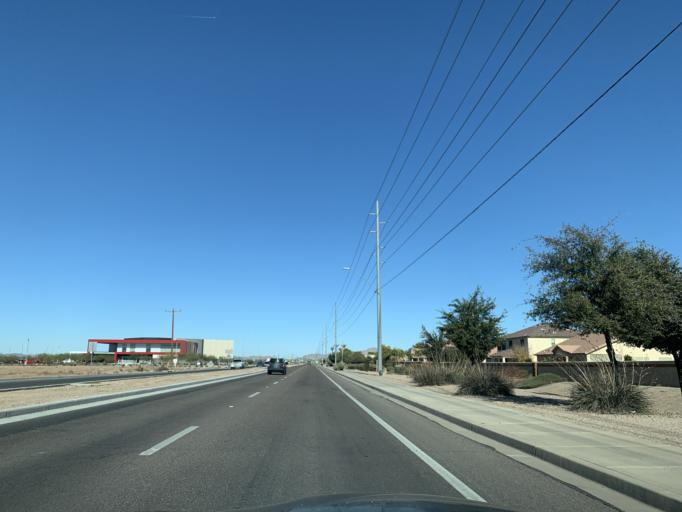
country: US
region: Arizona
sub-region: Pinal County
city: Casa Grande
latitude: 32.9032
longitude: -111.7224
